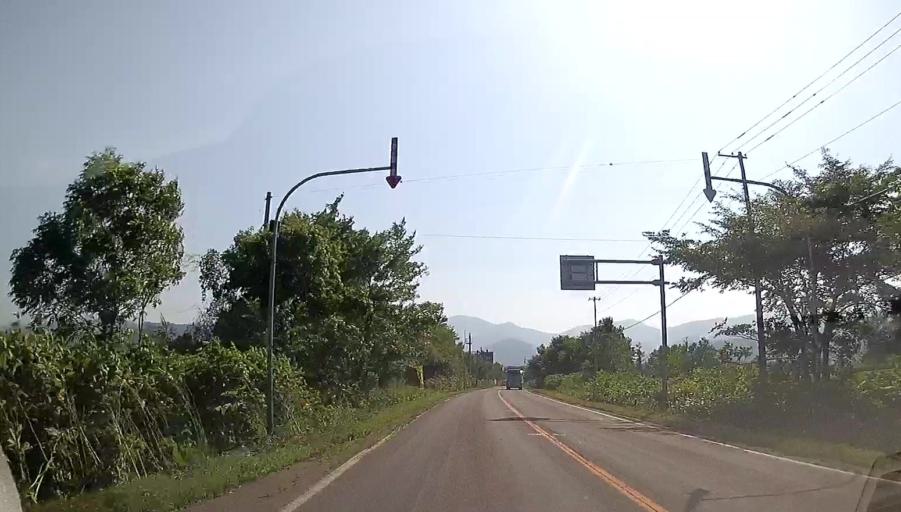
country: JP
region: Hokkaido
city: Otofuke
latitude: 42.9955
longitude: 142.8537
